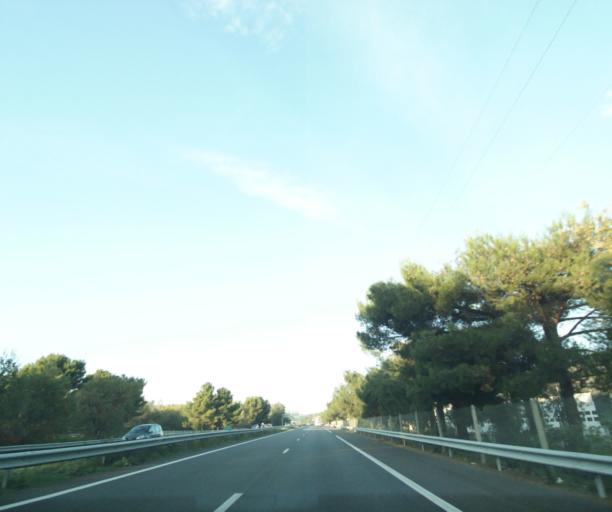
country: FR
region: Provence-Alpes-Cote d'Azur
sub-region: Departement des Bouches-du-Rhone
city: Aubagne
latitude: 43.2990
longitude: 5.5900
